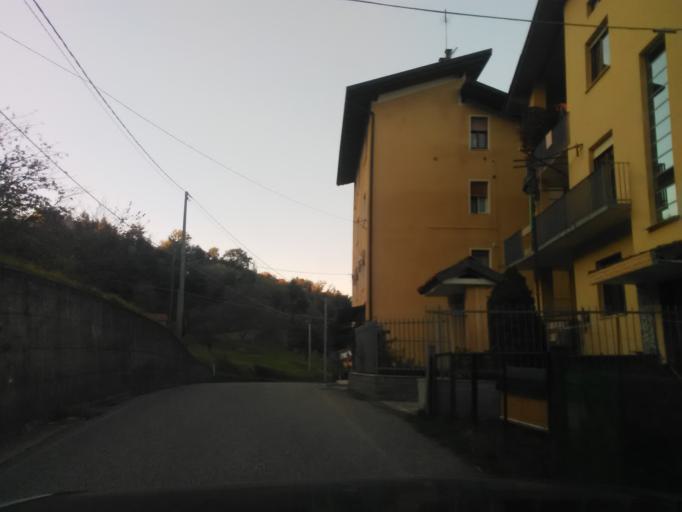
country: IT
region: Piedmont
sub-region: Provincia di Vercelli
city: Borgosesia
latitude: 45.7220
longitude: 8.2795
